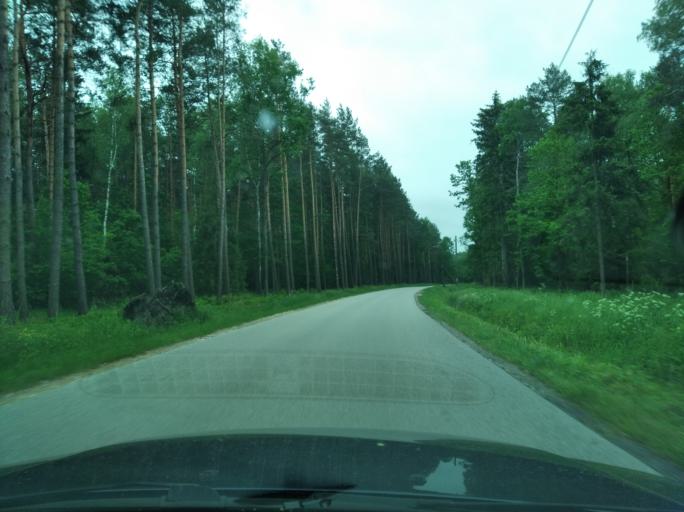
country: PL
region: Subcarpathian Voivodeship
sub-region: Powiat ropczycko-sedziszowski
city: Sedziszow Malopolski
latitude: 50.1295
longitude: 21.6714
